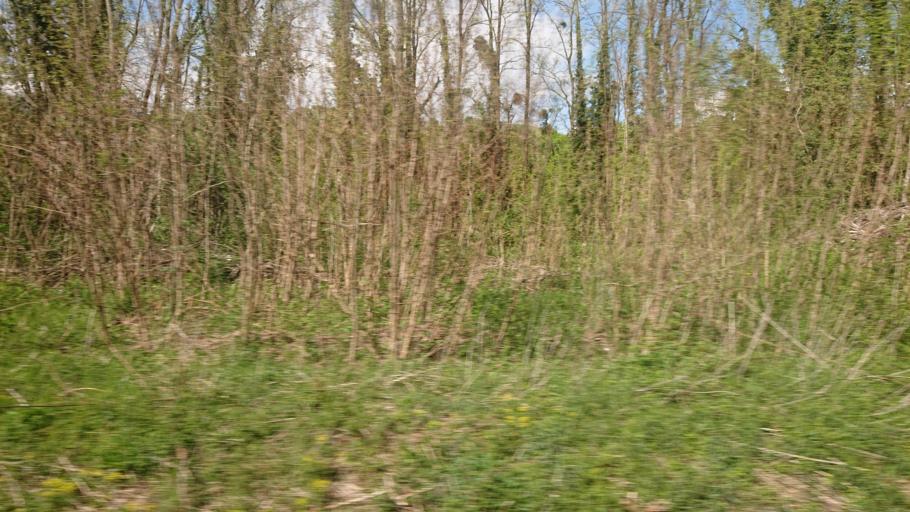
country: FR
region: Rhone-Alpes
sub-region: Departement de l'Ain
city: Collonges
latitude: 46.1353
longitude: 5.9336
